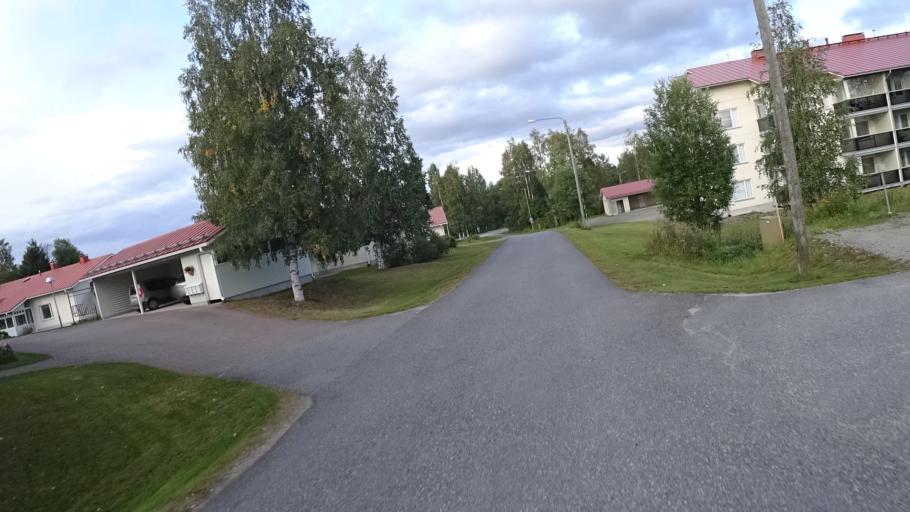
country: FI
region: North Karelia
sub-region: Joensuu
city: Ilomantsi
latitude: 62.6712
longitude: 30.9374
